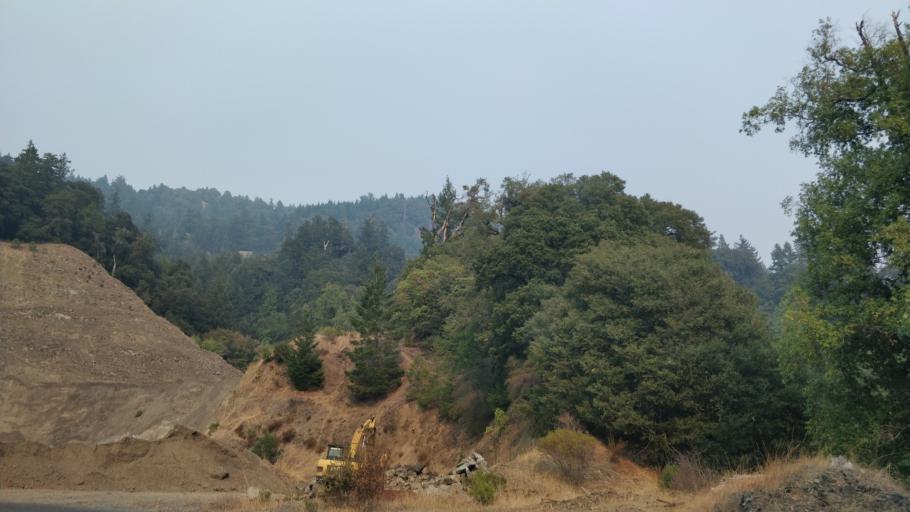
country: US
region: California
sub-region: Humboldt County
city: Rio Dell
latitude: 40.2471
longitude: -124.1209
